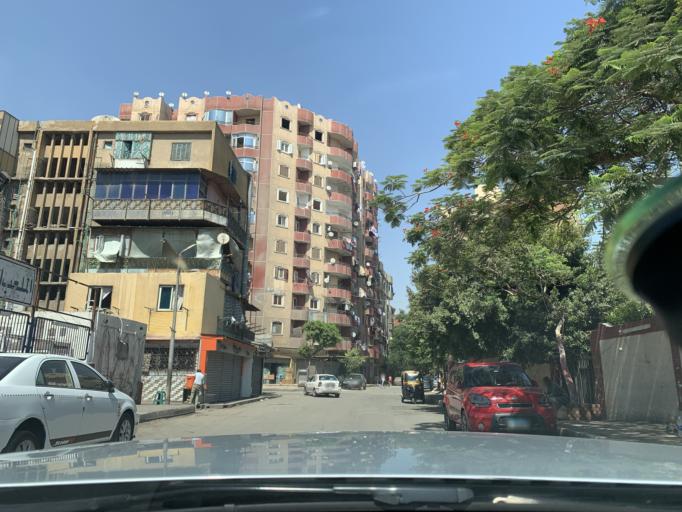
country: EG
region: Muhafazat al Qahirah
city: Cairo
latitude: 30.0758
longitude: 31.2580
